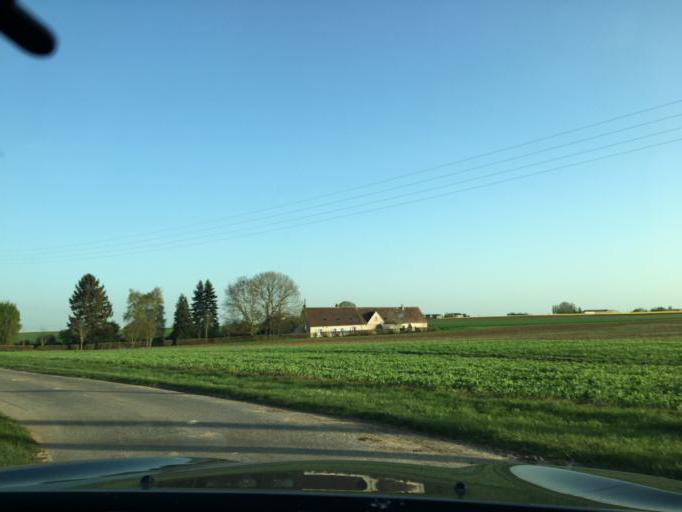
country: FR
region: Centre
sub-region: Departement du Loir-et-Cher
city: Ouzouer-le-Marche
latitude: 47.8417
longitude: 1.5284
